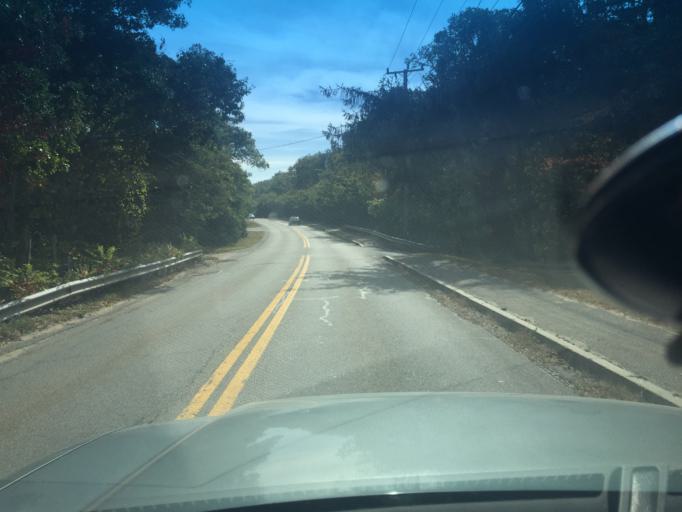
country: US
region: Massachusetts
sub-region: Barnstable County
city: North Falmouth
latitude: 41.6555
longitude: -70.6121
